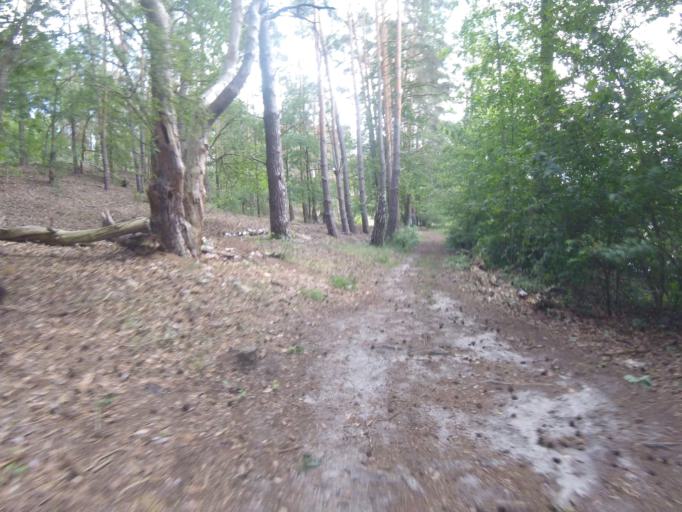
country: DE
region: Brandenburg
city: Bestensee
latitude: 52.2475
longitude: 13.6130
